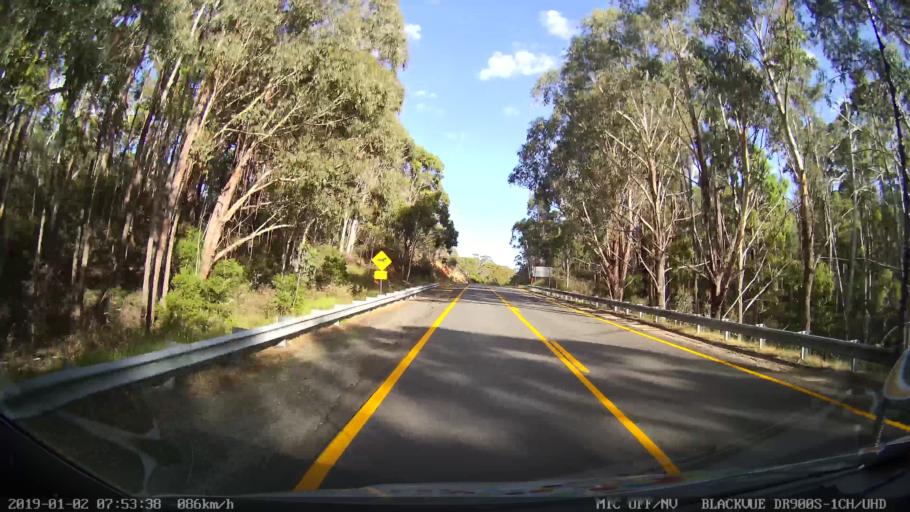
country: AU
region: New South Wales
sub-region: Tumut Shire
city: Tumut
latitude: -35.7028
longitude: 148.5037
